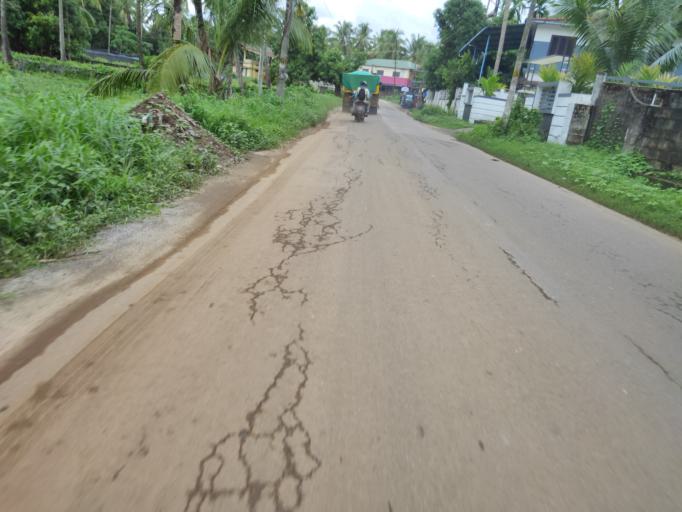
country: IN
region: Kerala
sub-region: Malappuram
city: Manjeri
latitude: 11.1976
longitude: 76.2210
